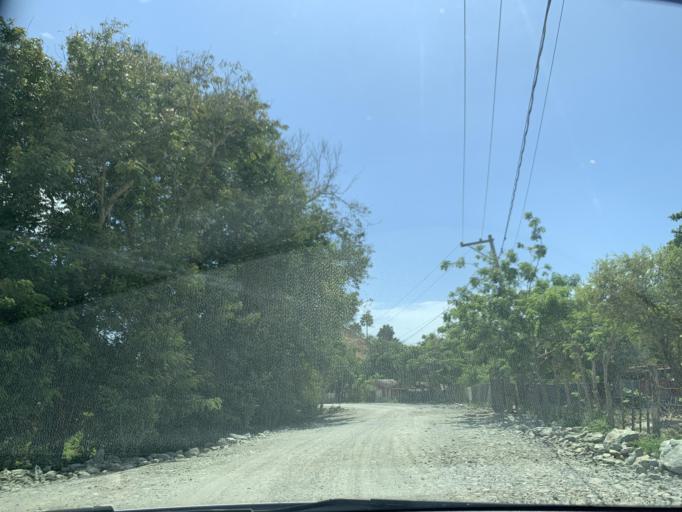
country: DO
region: Puerto Plata
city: Luperon
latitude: 19.8825
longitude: -70.8385
